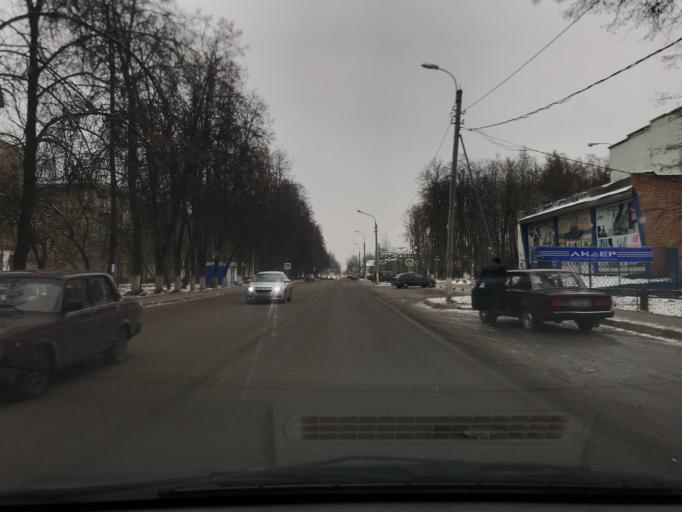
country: RU
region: Moskovskaya
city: Elektrostal'
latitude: 55.7925
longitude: 38.4461
